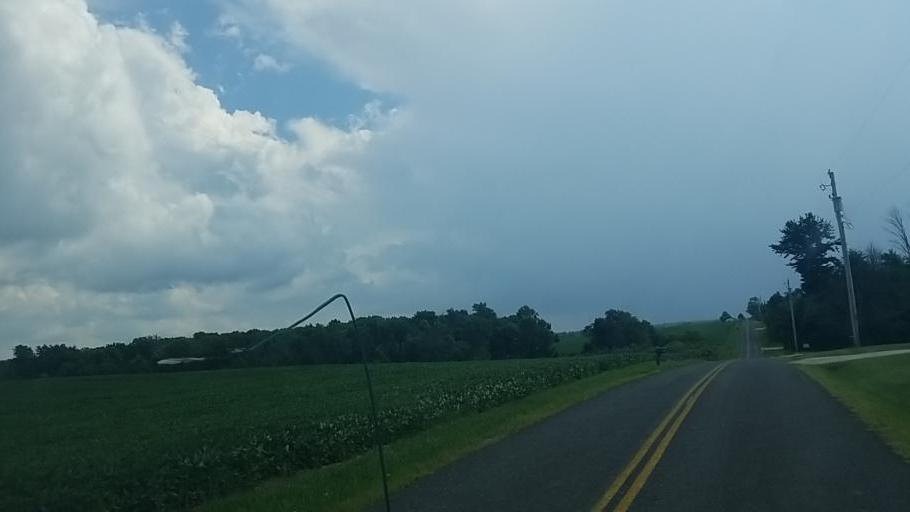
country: US
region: Ohio
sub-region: Medina County
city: Medina
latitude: 41.1326
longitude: -81.9624
